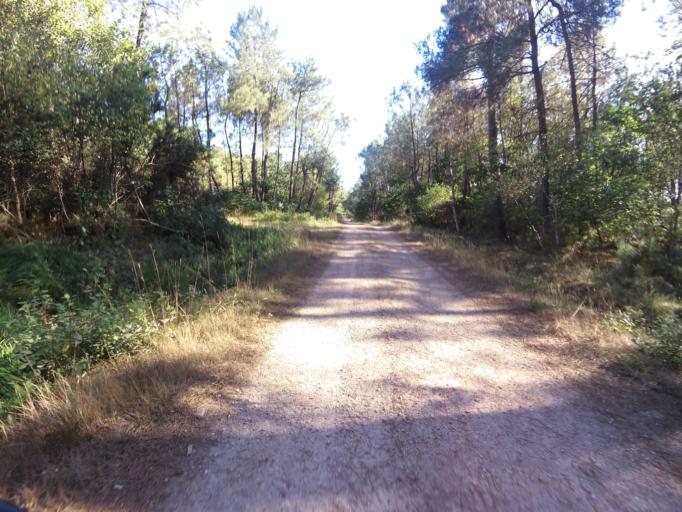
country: FR
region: Brittany
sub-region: Departement du Morbihan
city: Molac
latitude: 47.7081
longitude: -2.4175
